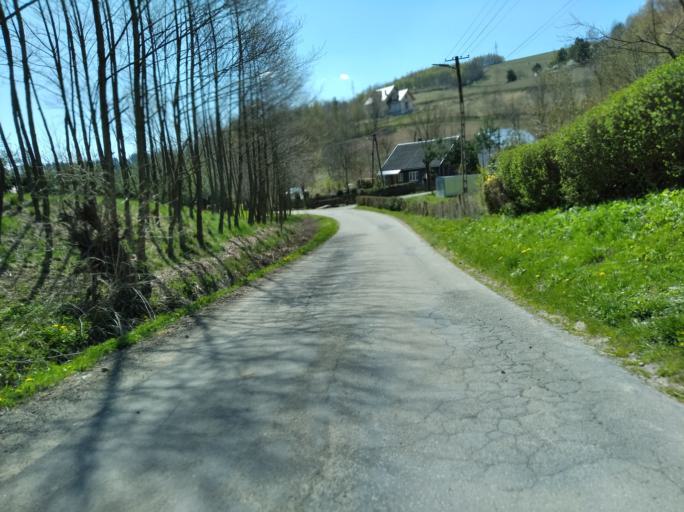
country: PL
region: Subcarpathian Voivodeship
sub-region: Powiat brzozowski
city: Dydnia
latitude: 49.7163
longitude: 22.1636
